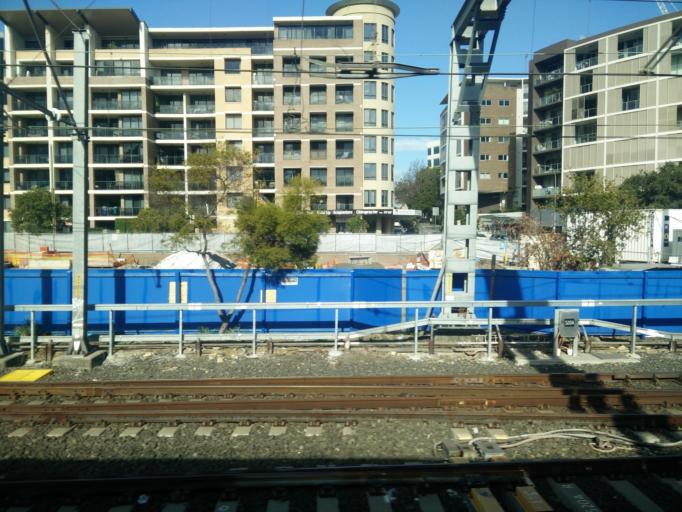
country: AU
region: New South Wales
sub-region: Ashfield
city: Ashfield
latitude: -33.8880
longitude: 151.1269
